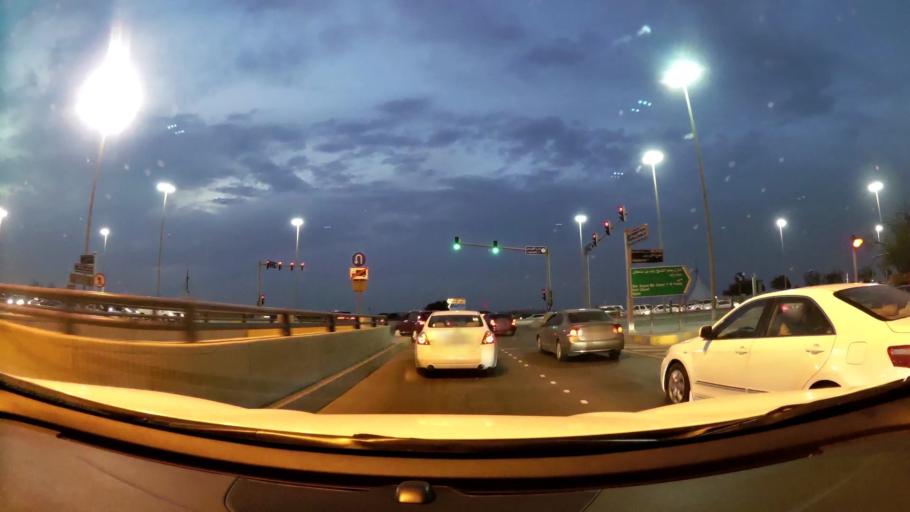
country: AE
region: Abu Dhabi
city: Abu Dhabi
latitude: 24.4952
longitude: 54.3589
